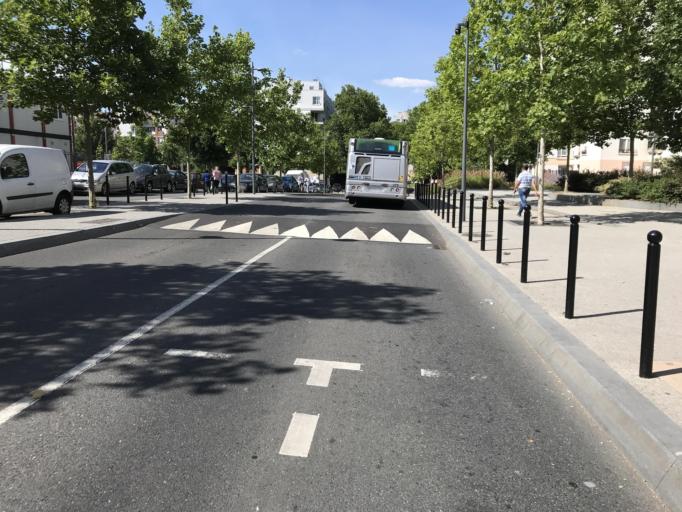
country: FR
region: Ile-de-France
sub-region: Departement de l'Essonne
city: Evry
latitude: 48.6343
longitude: 2.4295
